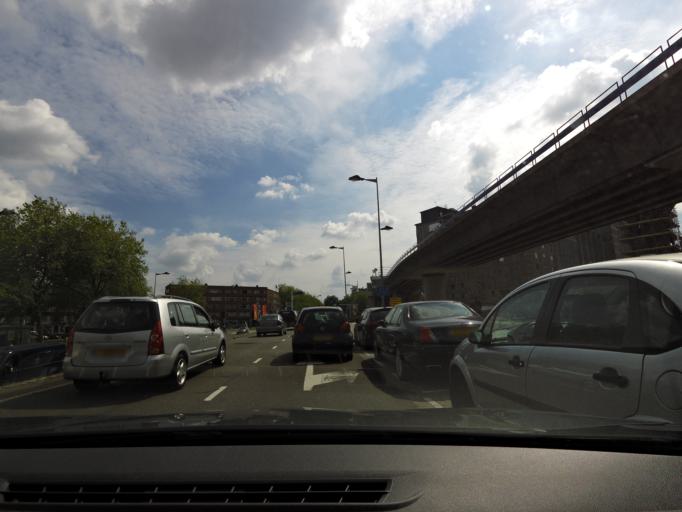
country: NL
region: South Holland
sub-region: Gemeente Rotterdam
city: Rotterdam
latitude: 51.8985
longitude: 4.4957
